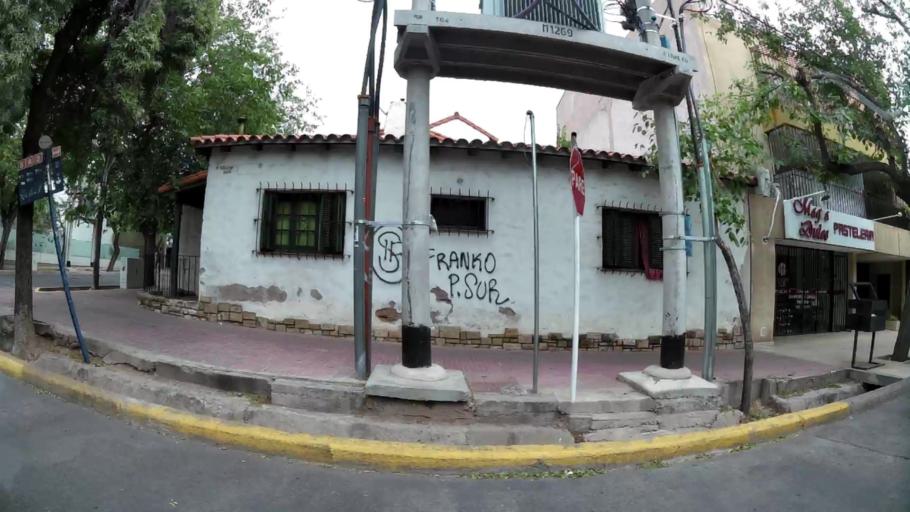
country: AR
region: Mendoza
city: Mendoza
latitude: -32.9004
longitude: -68.8572
